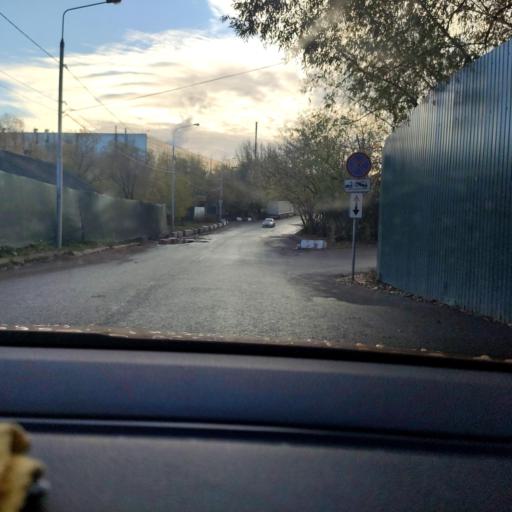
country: RU
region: Moscow
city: Ochakovo-Matveyevskoye
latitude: 55.6845
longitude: 37.4412
